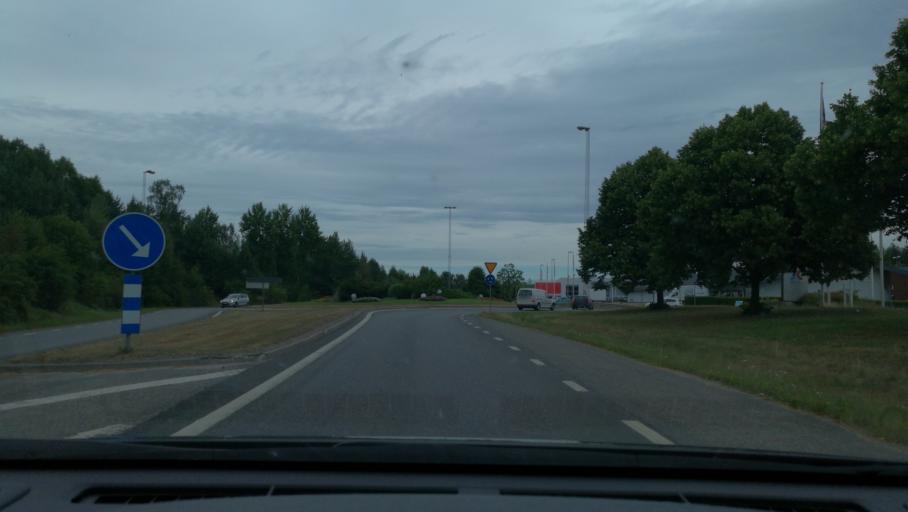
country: SE
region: Soedermanland
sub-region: Katrineholms Kommun
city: Katrineholm
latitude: 59.0011
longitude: 16.2223
